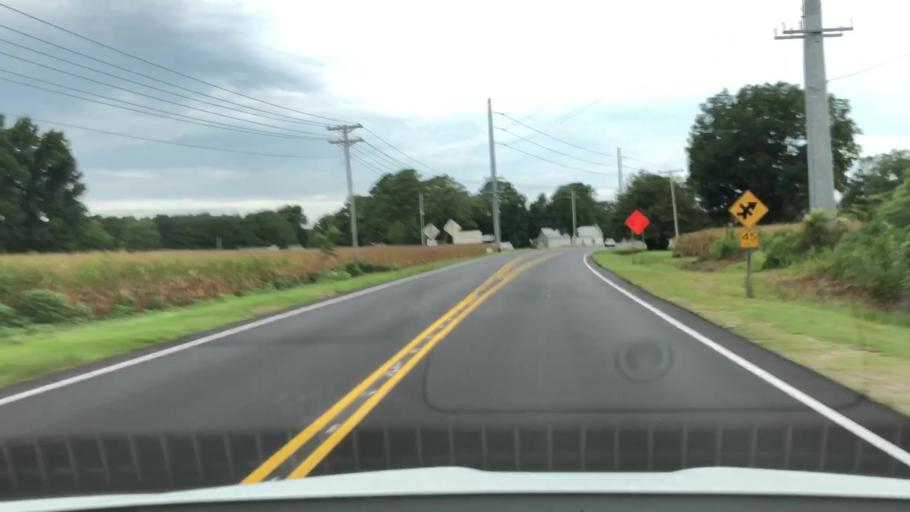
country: US
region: North Carolina
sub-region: Onslow County
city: Swansboro
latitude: 34.7893
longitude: -77.1274
